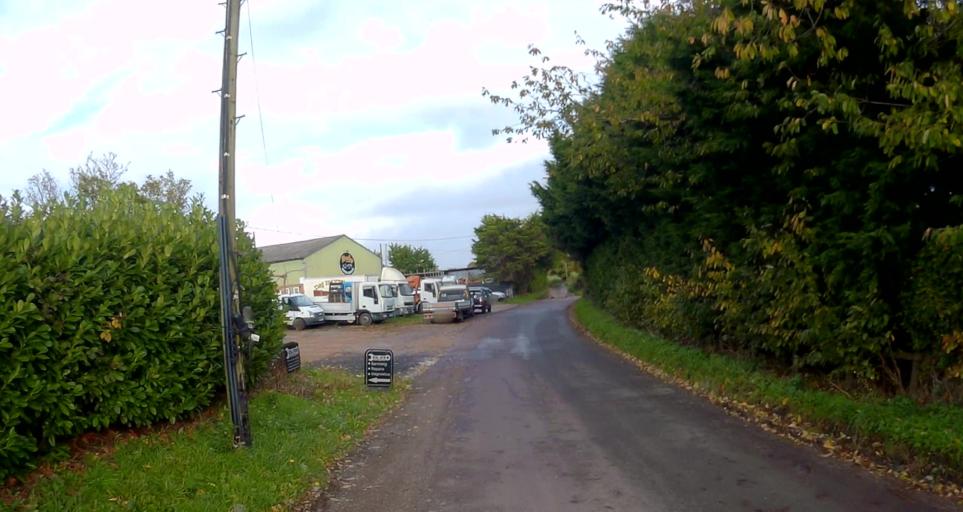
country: GB
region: England
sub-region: Hampshire
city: Four Marks
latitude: 51.1366
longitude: -1.1051
